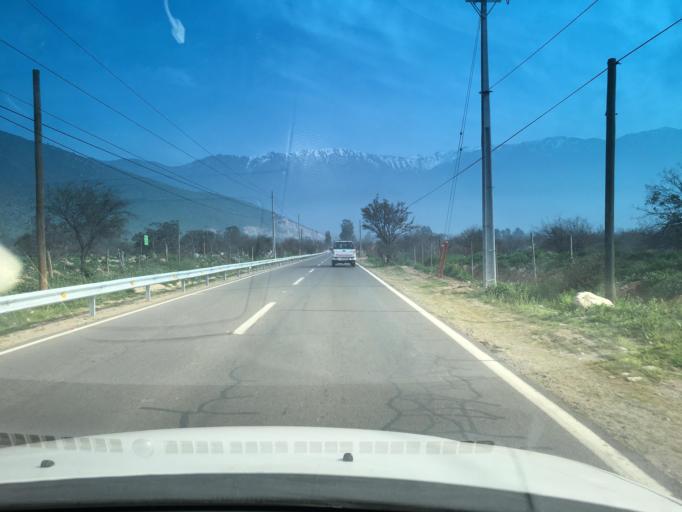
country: CL
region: Santiago Metropolitan
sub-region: Provincia de Chacabuco
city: Lampa
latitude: -33.2497
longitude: -70.9099
